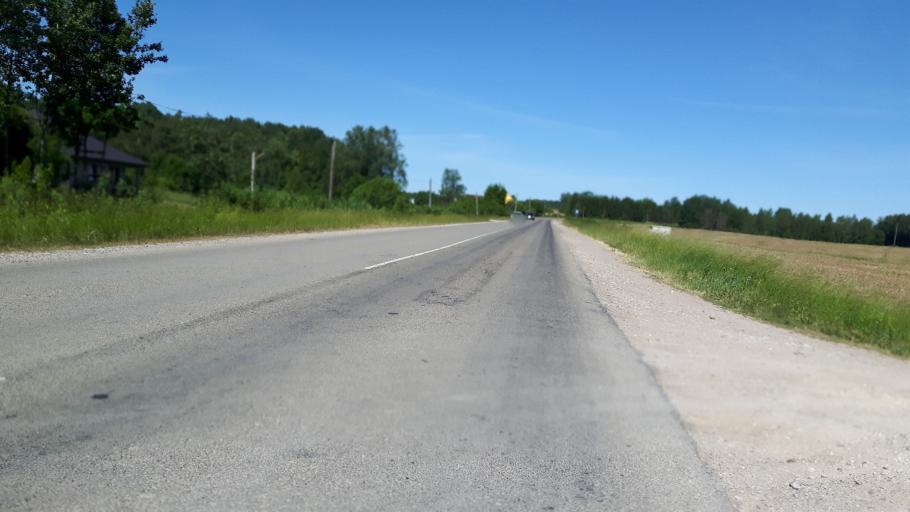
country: LV
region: Tukuma Rajons
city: Tukums
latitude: 56.9736
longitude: 23.1260
